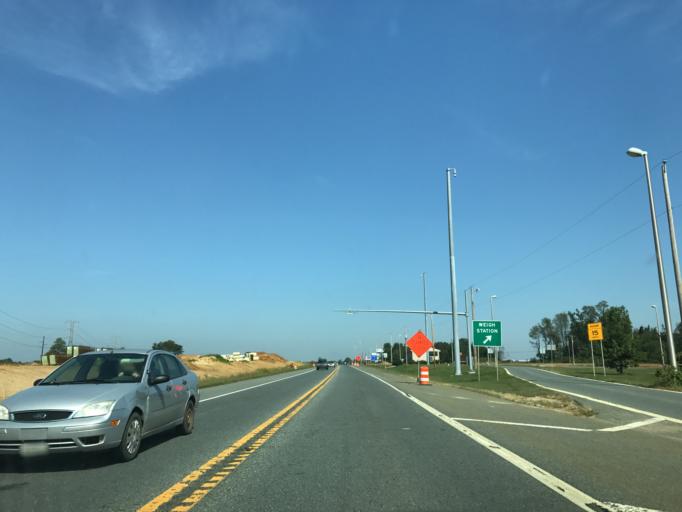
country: US
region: Delaware
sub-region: New Castle County
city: Middletown
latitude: 39.4182
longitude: -75.7648
